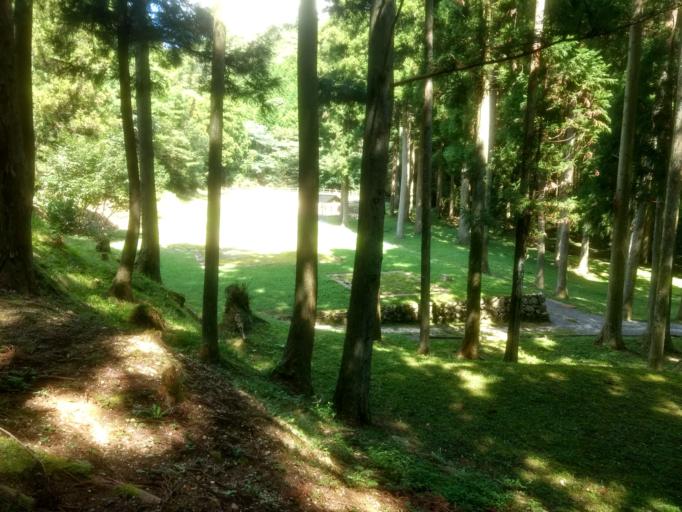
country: JP
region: Yamaguchi
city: Hagi
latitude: 34.5054
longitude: 131.5381
